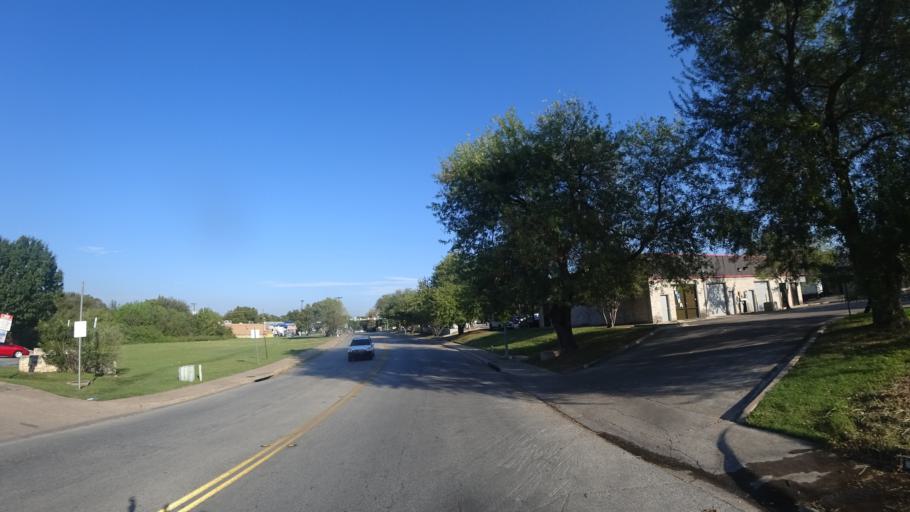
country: US
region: Texas
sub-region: Travis County
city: Austin
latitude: 30.3089
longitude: -97.6661
